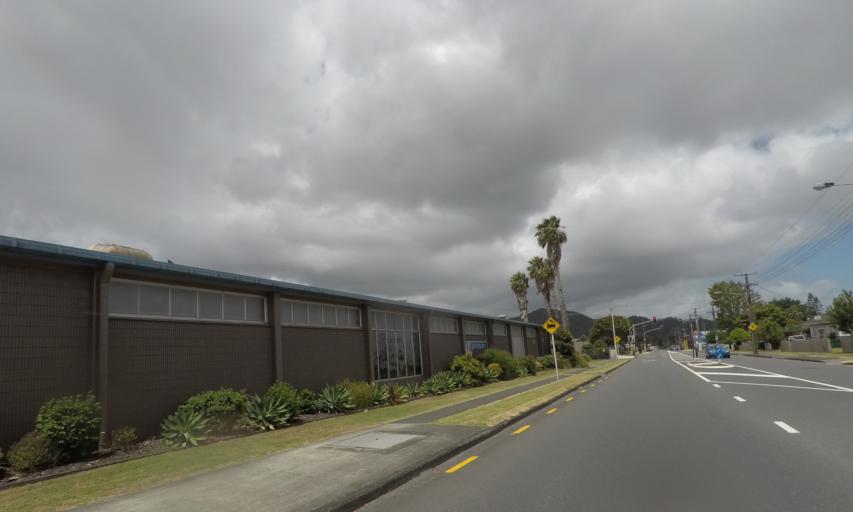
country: NZ
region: Northland
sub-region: Whangarei
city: Whangarei
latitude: -35.7032
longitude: 174.3164
